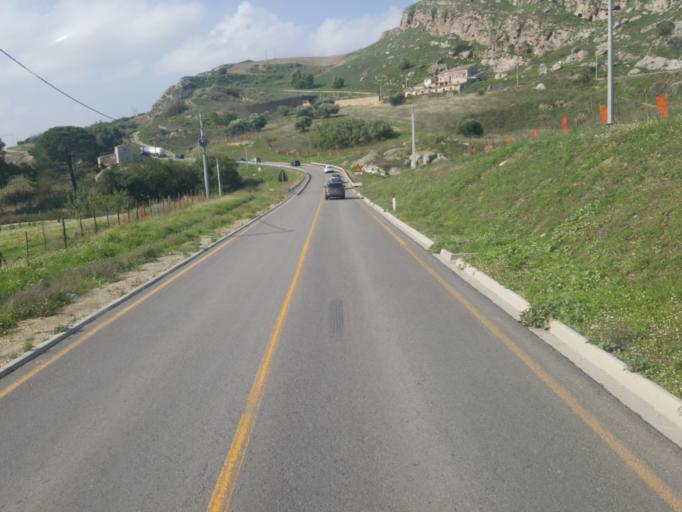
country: IT
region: Sicily
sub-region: Provincia di Caltanissetta
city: San Cataldo
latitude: 37.4503
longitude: 13.9610
